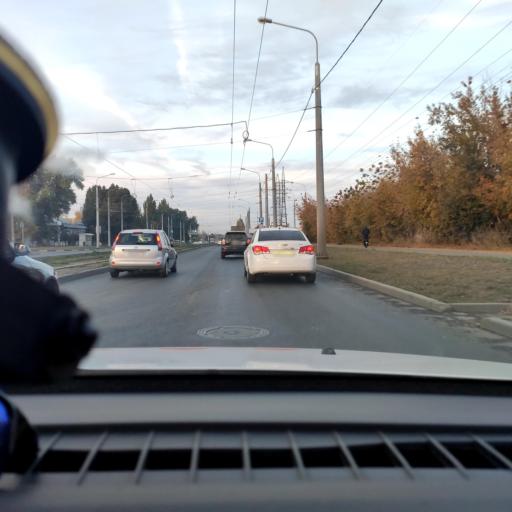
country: RU
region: Samara
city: Samara
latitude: 53.2035
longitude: 50.2672
